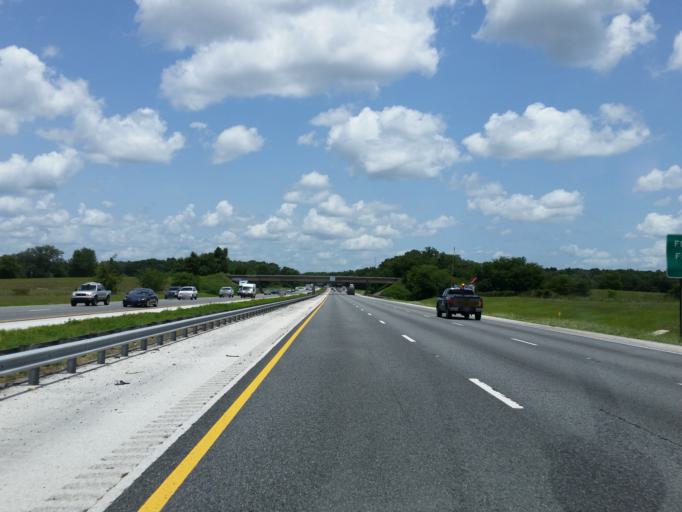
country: US
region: Florida
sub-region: Marion County
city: Ocala
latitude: 29.2498
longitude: -82.1898
